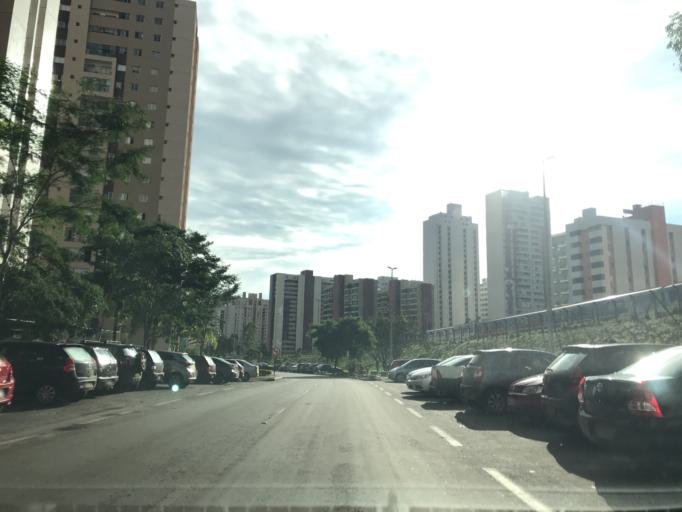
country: BR
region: Federal District
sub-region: Brasilia
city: Brasilia
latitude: -15.8397
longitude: -48.0256
